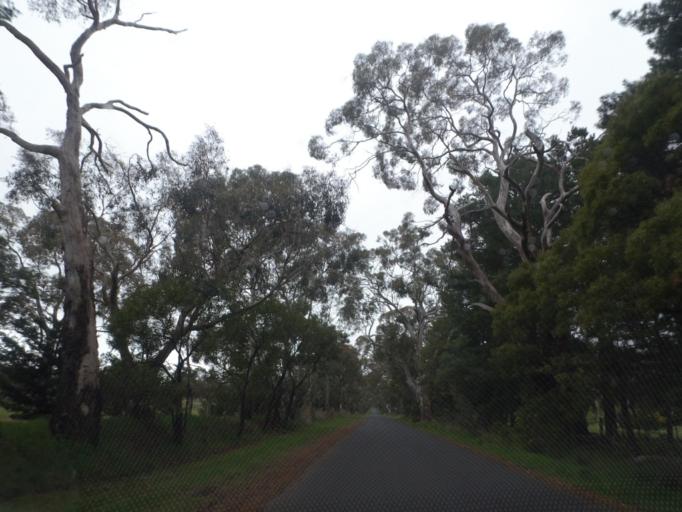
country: AU
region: Victoria
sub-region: Hume
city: Sunbury
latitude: -37.3268
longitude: 144.5882
